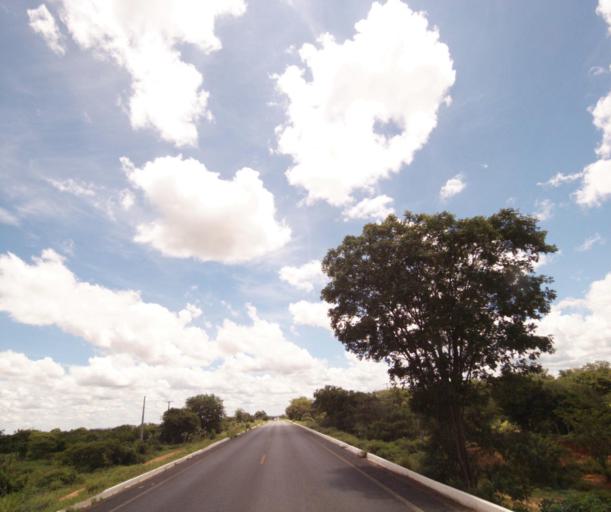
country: BR
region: Bahia
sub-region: Bom Jesus Da Lapa
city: Bom Jesus da Lapa
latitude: -13.2584
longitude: -43.4760
